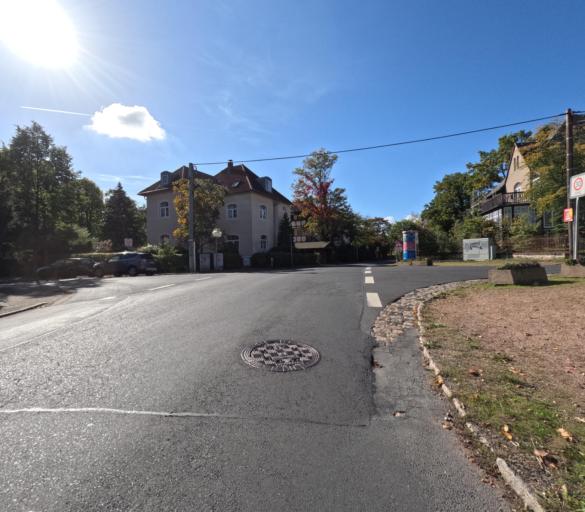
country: DE
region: Saxony
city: Radebeul
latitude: 51.1343
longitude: 13.6481
